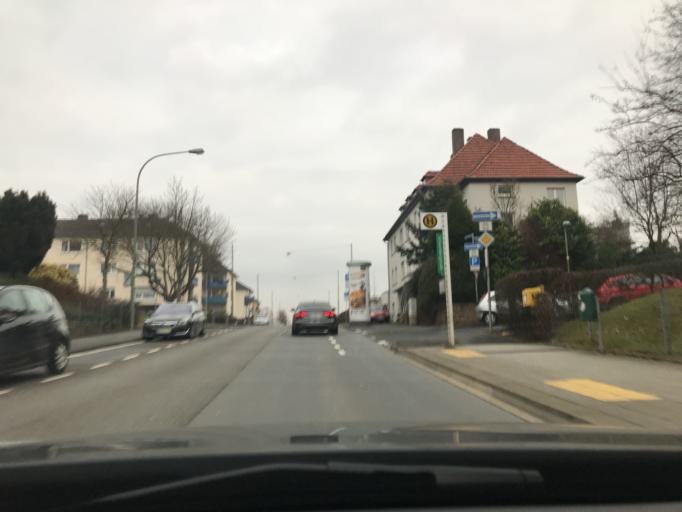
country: DE
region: Hesse
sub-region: Regierungsbezirk Kassel
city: Kassel
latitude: 51.3306
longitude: 9.5076
